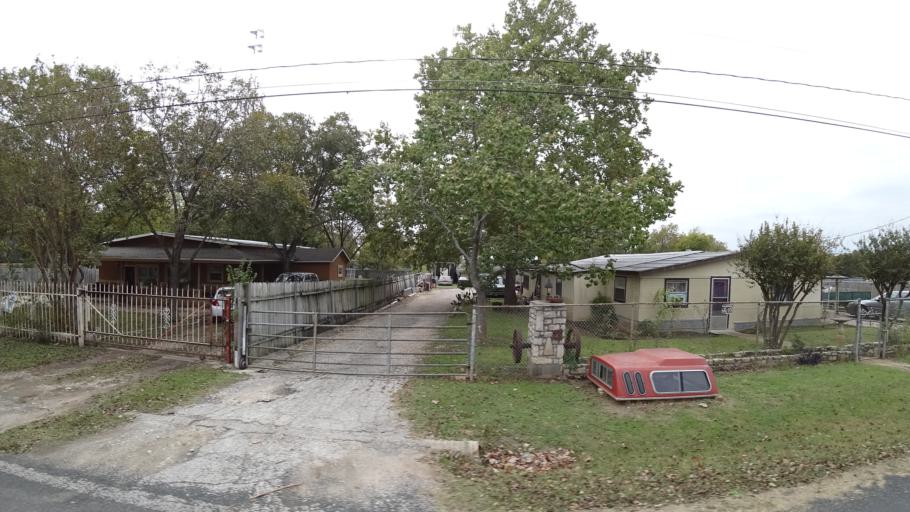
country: US
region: Texas
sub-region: Travis County
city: Wells Branch
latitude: 30.4362
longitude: -97.6911
